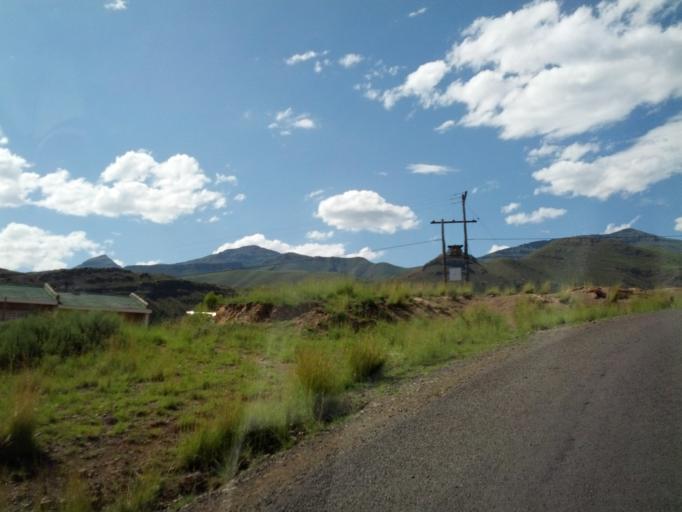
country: LS
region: Qacha's Nek
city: Qacha's Nek
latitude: -30.0565
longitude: 28.4788
